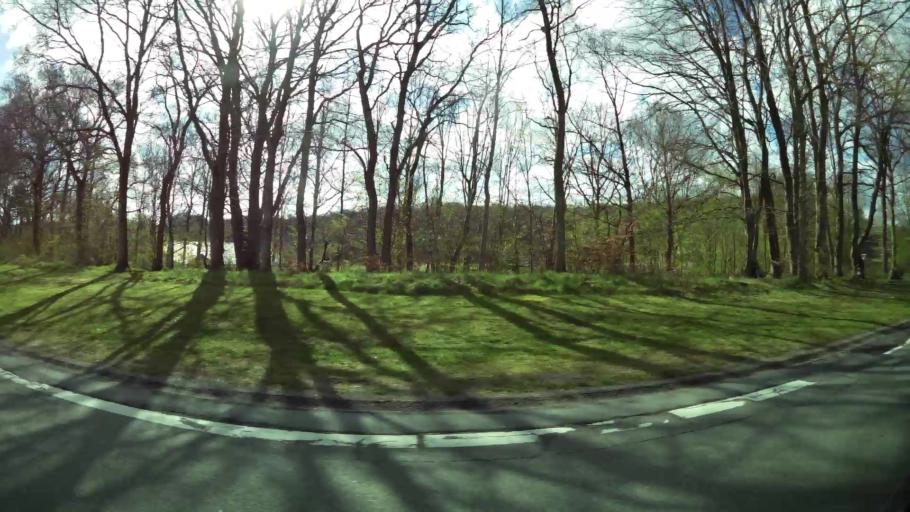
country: DK
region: North Denmark
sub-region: Mariagerfjord Kommune
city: Mariager
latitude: 56.6457
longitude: 9.9693
